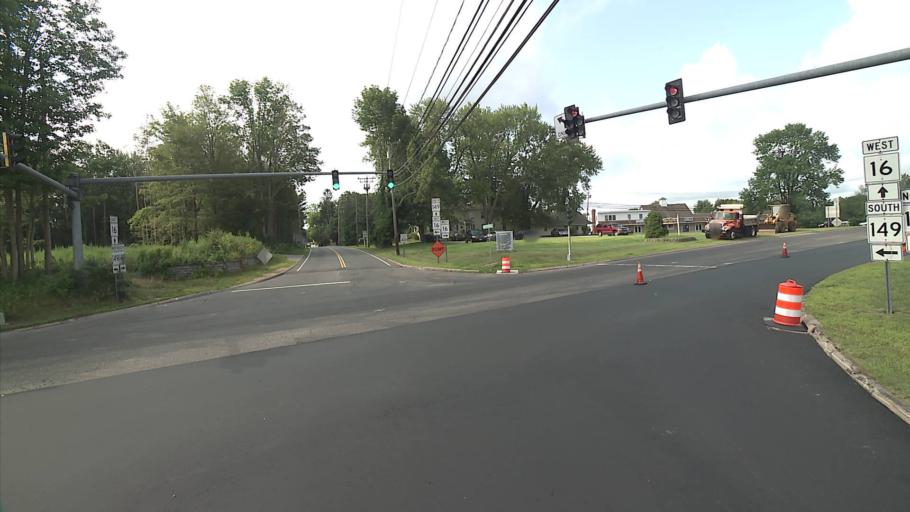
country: US
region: Connecticut
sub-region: Middlesex County
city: Moodus
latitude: 41.5456
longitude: -72.4131
